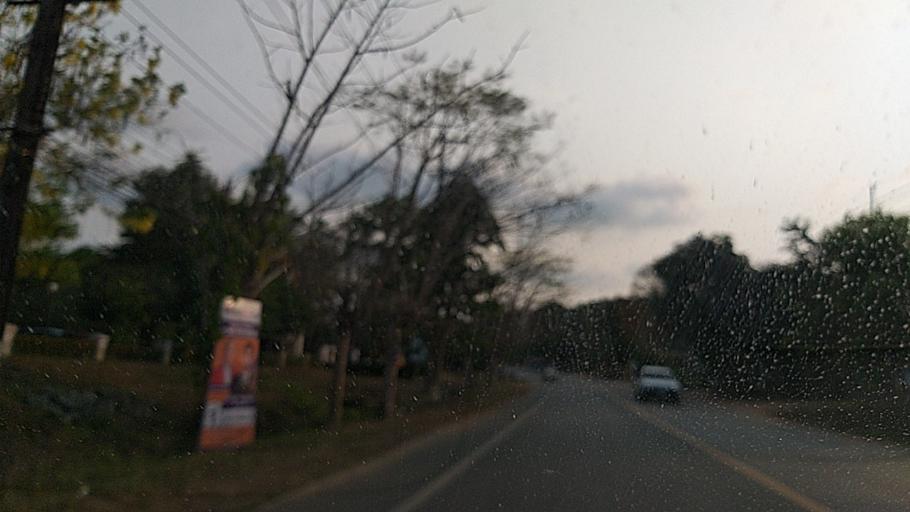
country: TH
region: Trat
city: Khao Saming
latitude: 12.2871
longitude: 102.3124
